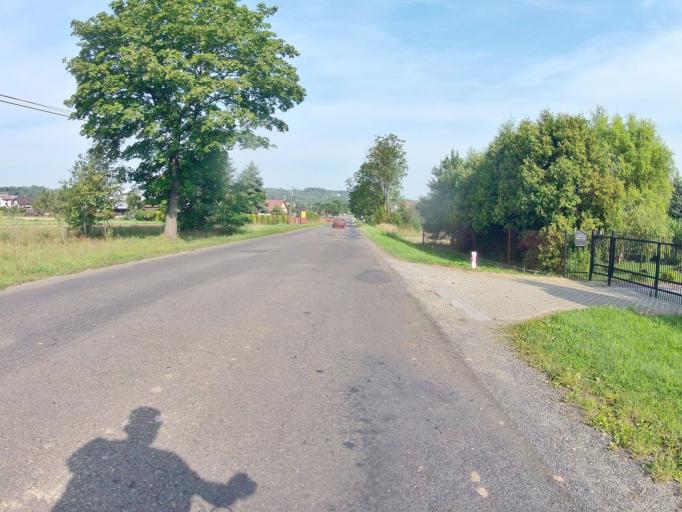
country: PL
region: Subcarpathian Voivodeship
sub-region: Powiat jasielski
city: Brzyska
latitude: 49.7876
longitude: 21.4012
